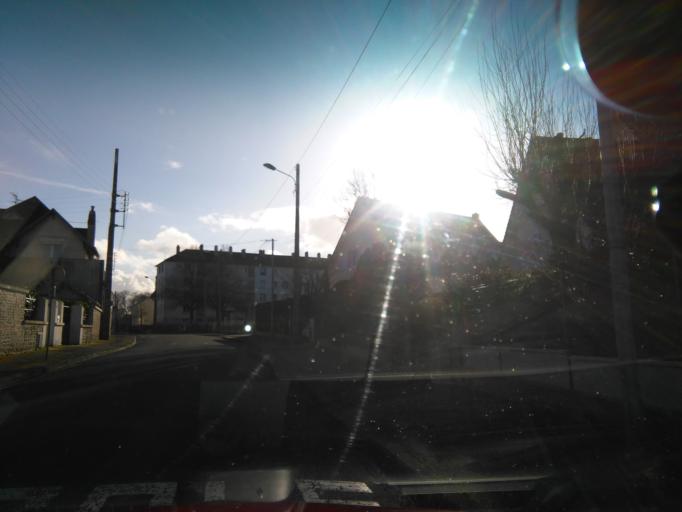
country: FR
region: Lower Normandy
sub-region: Departement du Calvados
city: Saint-Germain-la-Blanche-Herbe
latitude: 49.1782
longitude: -0.3860
